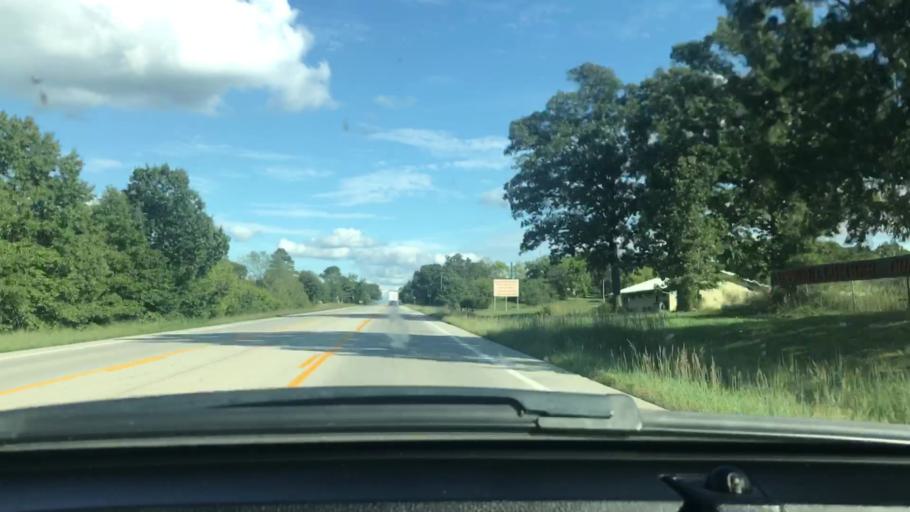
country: US
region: Missouri
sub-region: Howell County
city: West Plains
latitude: 36.6533
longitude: -91.6937
